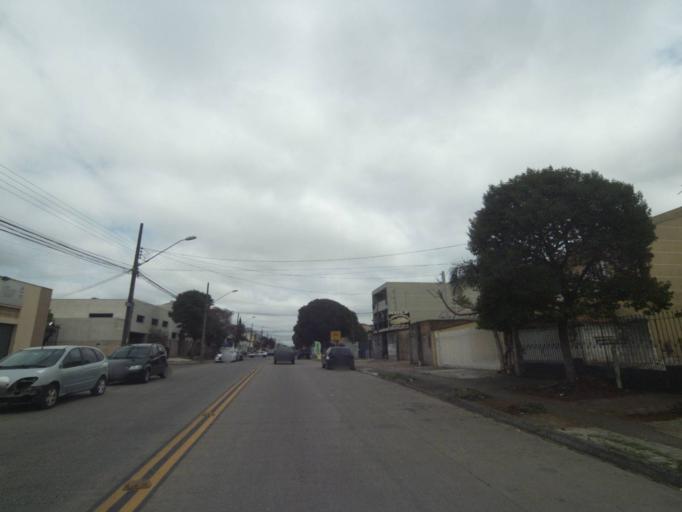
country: BR
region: Parana
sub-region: Sao Jose Dos Pinhais
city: Sao Jose dos Pinhais
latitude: -25.5475
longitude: -49.2544
